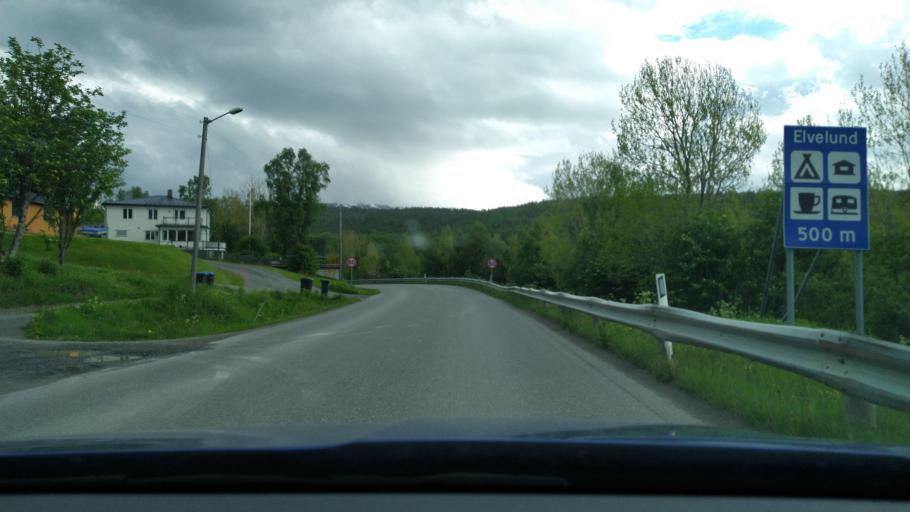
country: NO
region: Troms
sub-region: Salangen
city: Sjovegan
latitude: 68.8684
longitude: 17.8528
